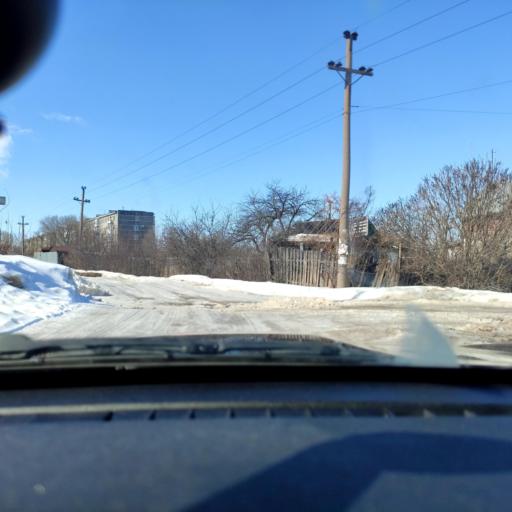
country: RU
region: Samara
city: Tol'yatti
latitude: 53.5664
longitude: 49.3128
